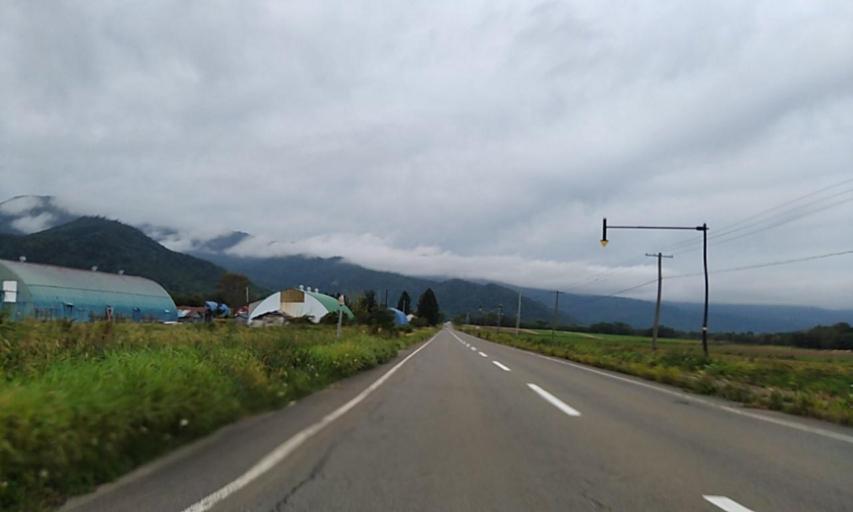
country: JP
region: Hokkaido
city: Bihoro
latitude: 43.5725
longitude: 144.2962
